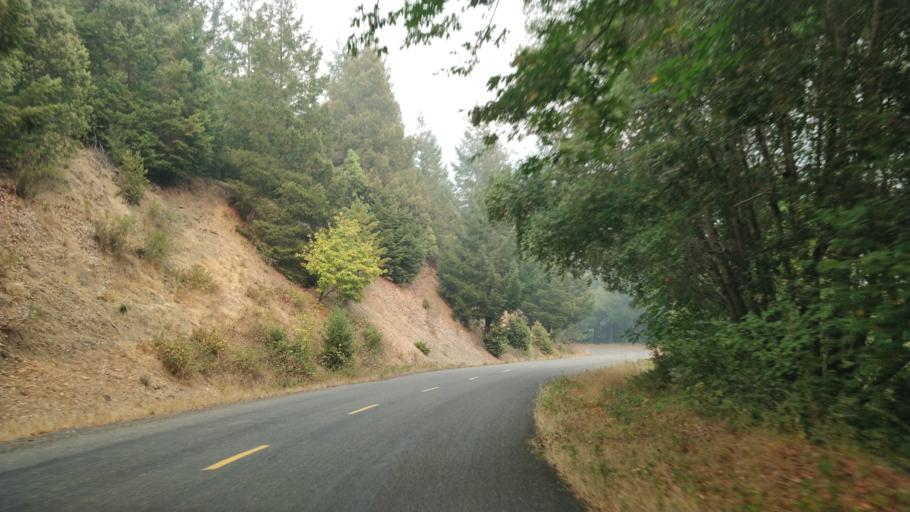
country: US
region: California
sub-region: Humboldt County
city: Rio Dell
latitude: 40.3314
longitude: -124.0305
